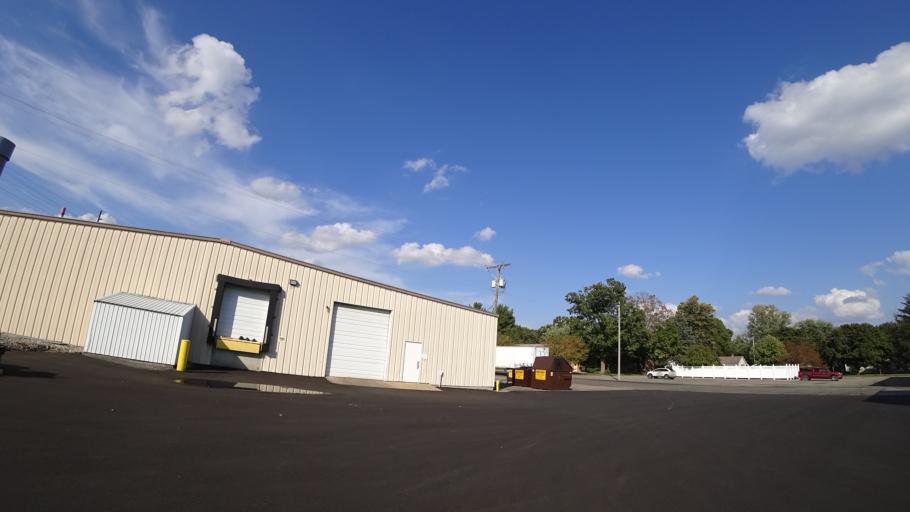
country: US
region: Michigan
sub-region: Saint Joseph County
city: Three Rivers
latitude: 41.9561
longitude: -85.6387
